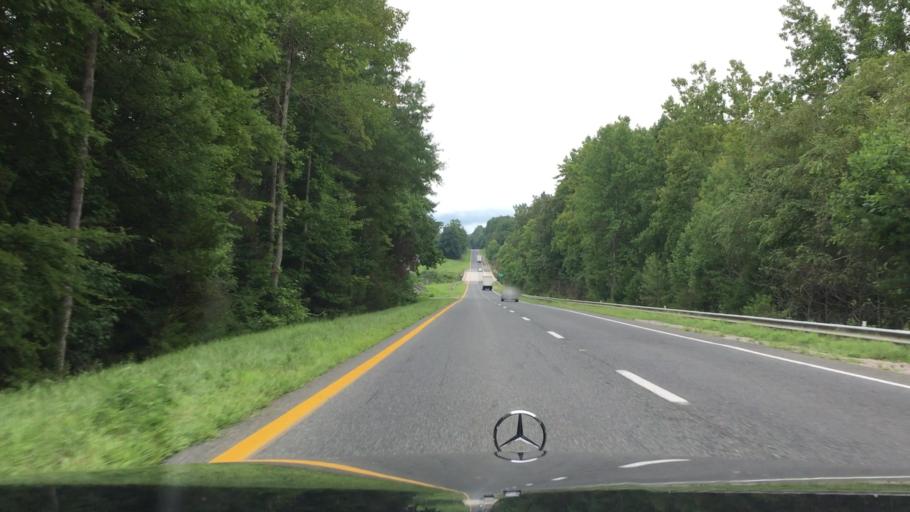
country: US
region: Virginia
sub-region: Prince Edward County
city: Farmville
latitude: 37.2985
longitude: -78.4430
